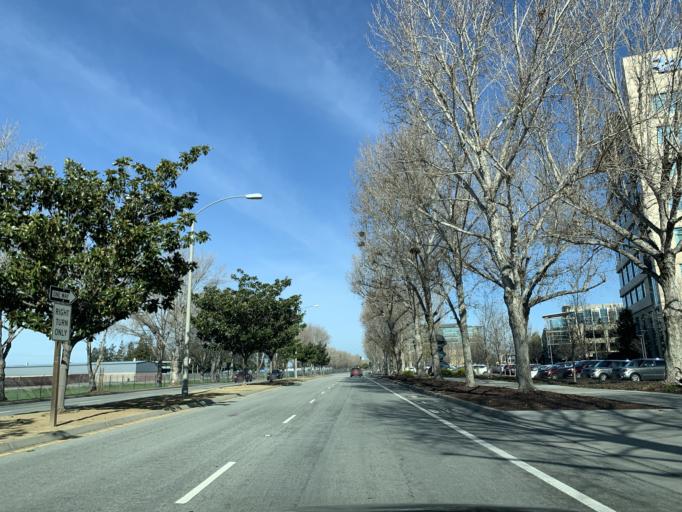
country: US
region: California
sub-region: Santa Clara County
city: Sunnyvale
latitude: 37.4038
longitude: -122.0368
